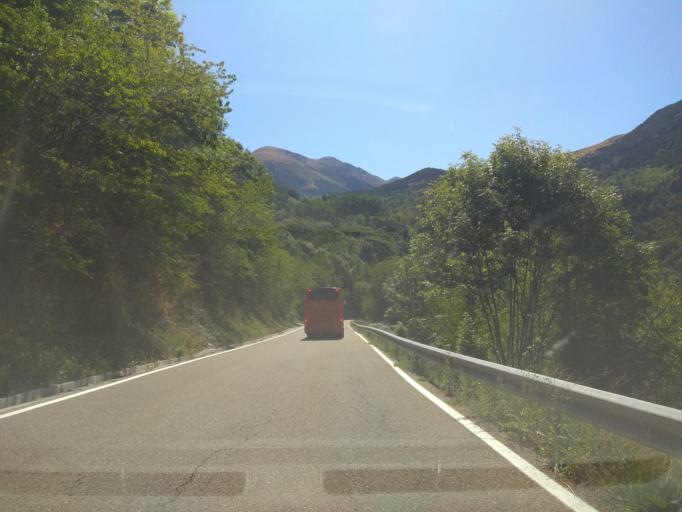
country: ES
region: Catalonia
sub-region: Provincia de Lleida
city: Vielha
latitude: 42.5218
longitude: 0.8418
